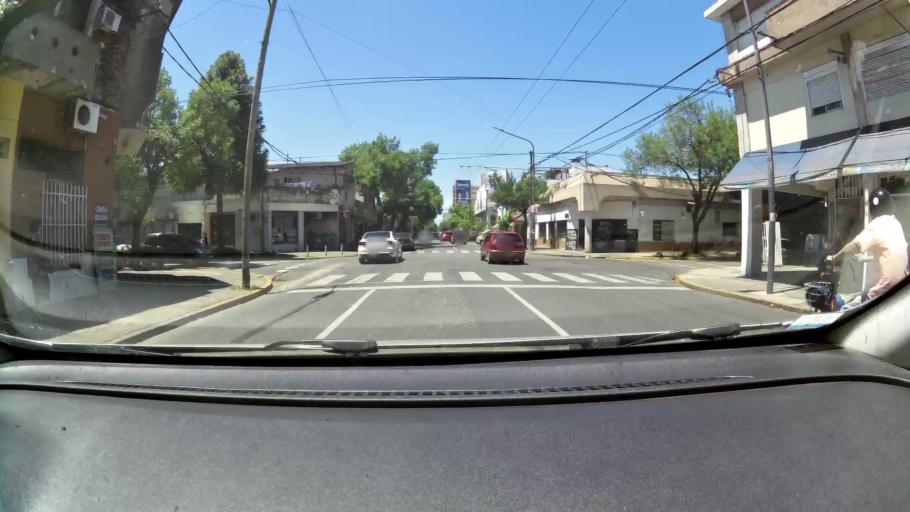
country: AR
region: Santa Fe
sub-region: Departamento de Rosario
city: Rosario
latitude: -32.9428
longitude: -60.6888
